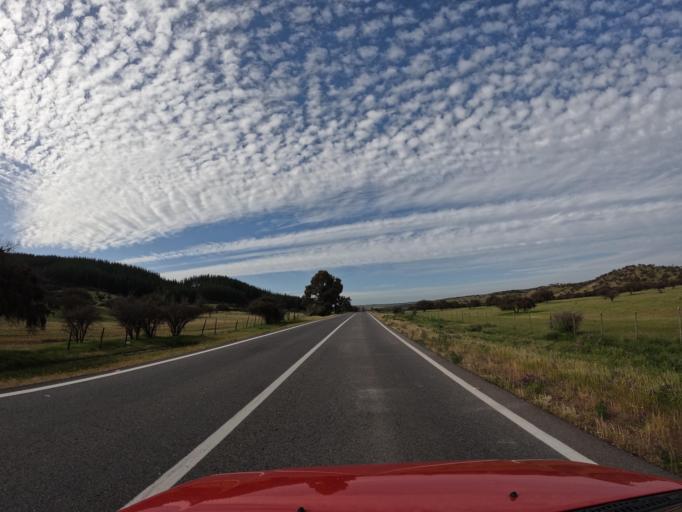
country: CL
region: O'Higgins
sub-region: Provincia de Colchagua
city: Santa Cruz
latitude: -34.3051
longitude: -71.7362
